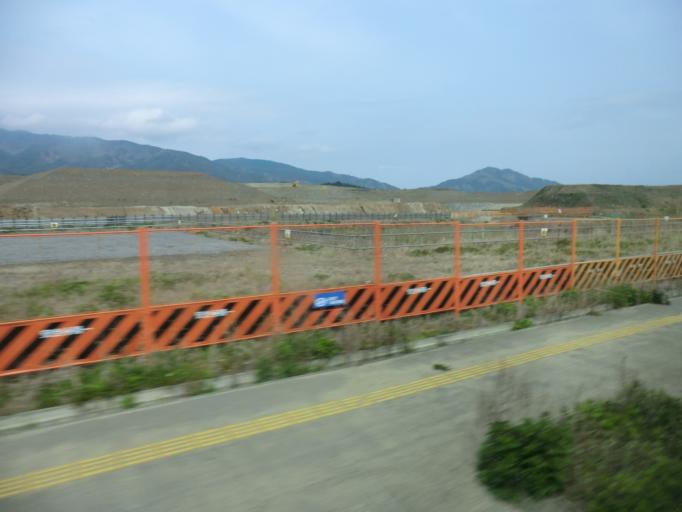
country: JP
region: Iwate
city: Ofunato
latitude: 39.0145
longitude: 141.6197
